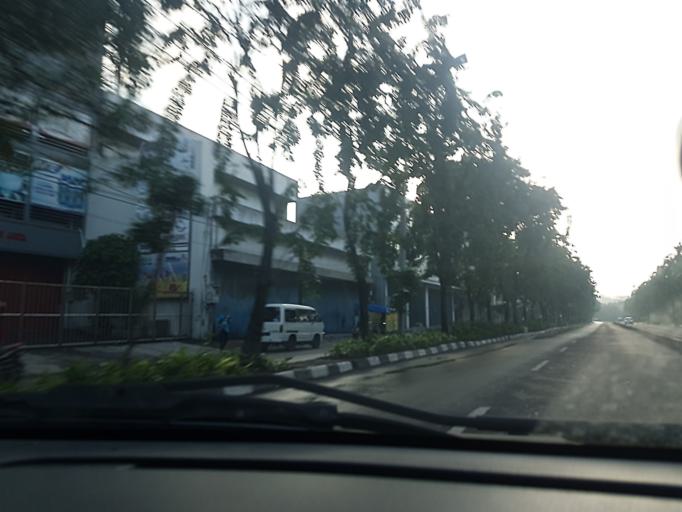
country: ID
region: East Java
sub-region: Kota Surabaya
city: Surabaya
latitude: -7.2451
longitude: 112.7230
